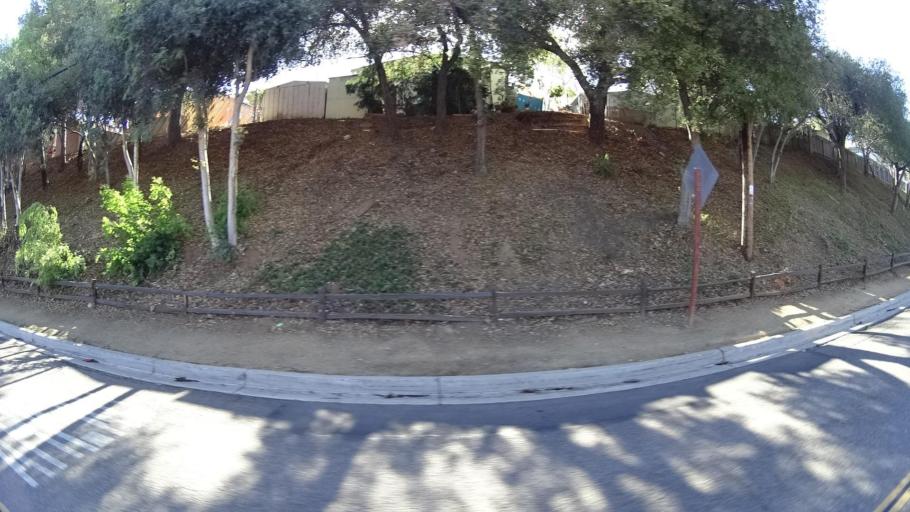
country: US
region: California
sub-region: San Diego County
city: Winter Gardens
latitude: 32.8311
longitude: -116.9063
